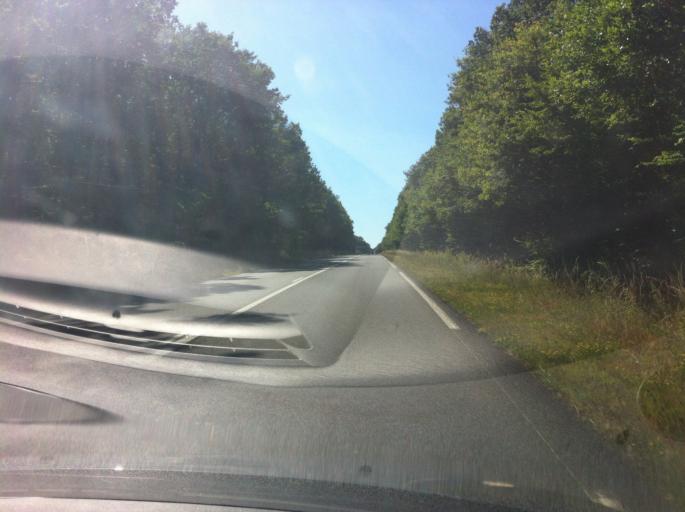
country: FR
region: Auvergne
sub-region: Departement de l'Allier
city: Chantelle
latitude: 46.3222
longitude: 3.0924
